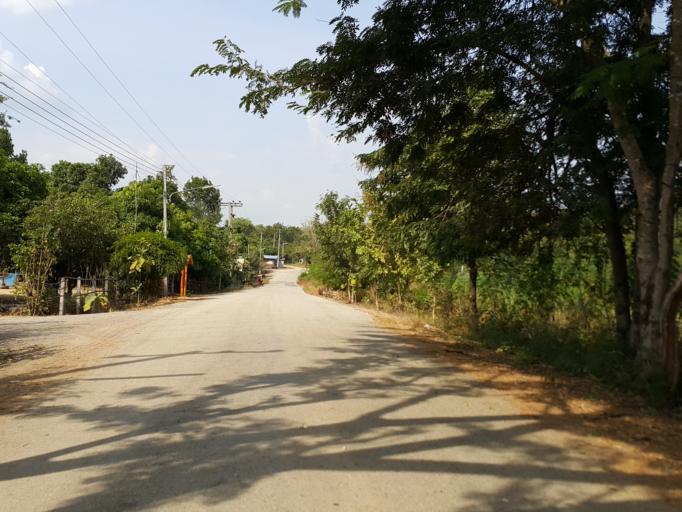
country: TH
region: Sukhothai
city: Thung Saliam
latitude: 17.3459
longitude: 99.4380
